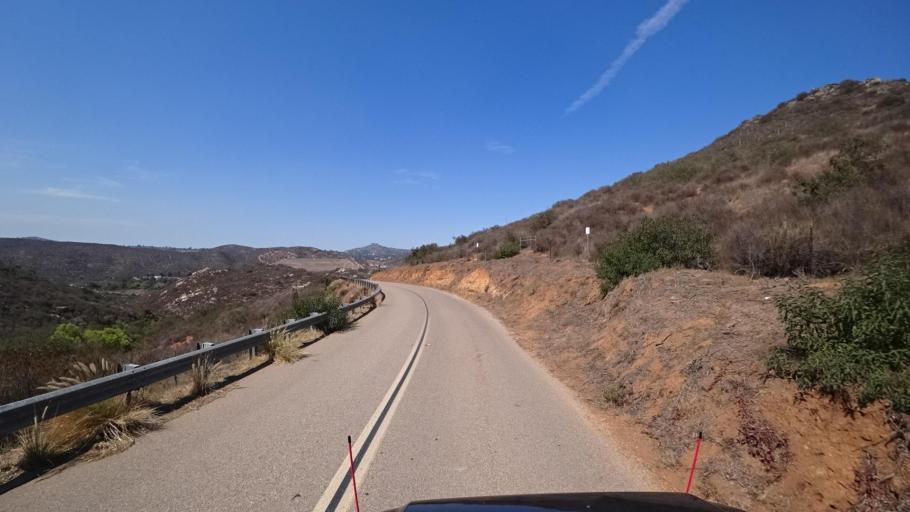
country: US
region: California
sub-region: San Diego County
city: Rancho San Diego
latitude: 32.7250
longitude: -116.9336
